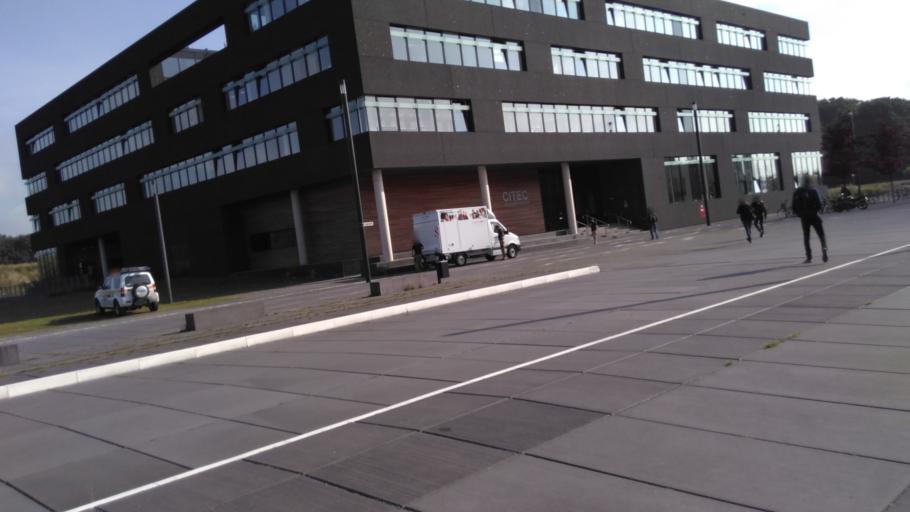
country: DE
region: North Rhine-Westphalia
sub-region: Regierungsbezirk Detmold
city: Bielefeld
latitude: 52.0447
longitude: 8.4920
